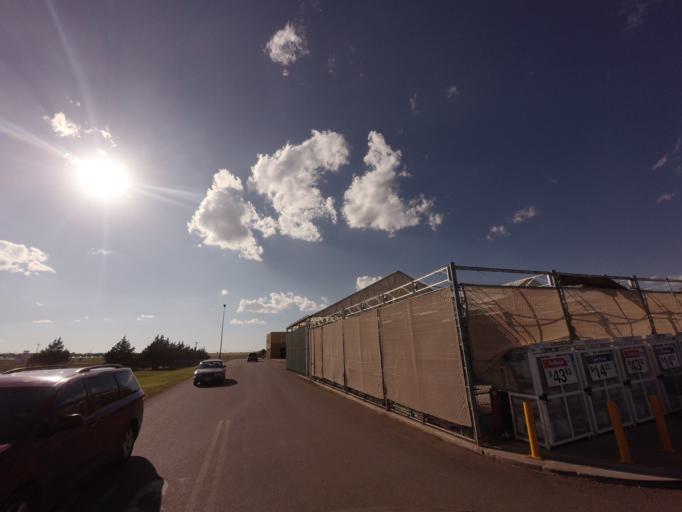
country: US
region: New Mexico
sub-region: Curry County
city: Clovis
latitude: 34.4367
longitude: -103.1997
